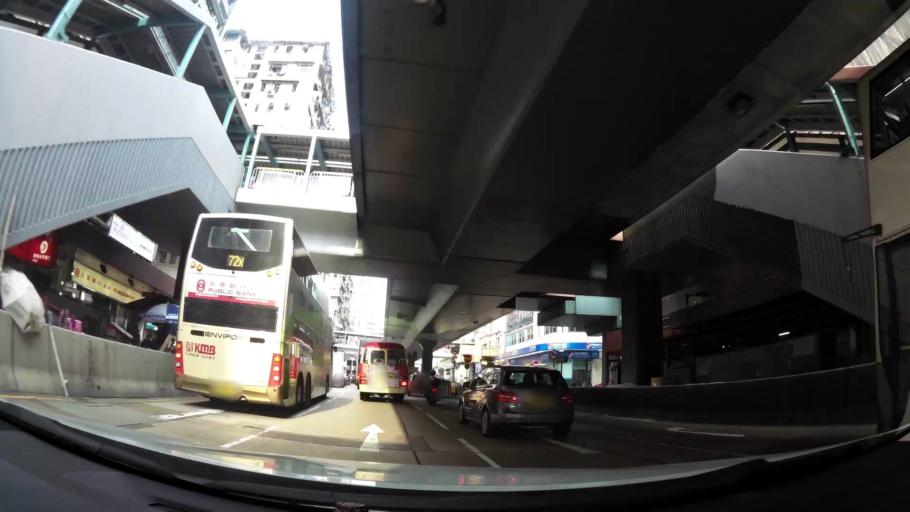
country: HK
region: Sham Shui Po
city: Sham Shui Po
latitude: 22.3210
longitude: 114.1690
